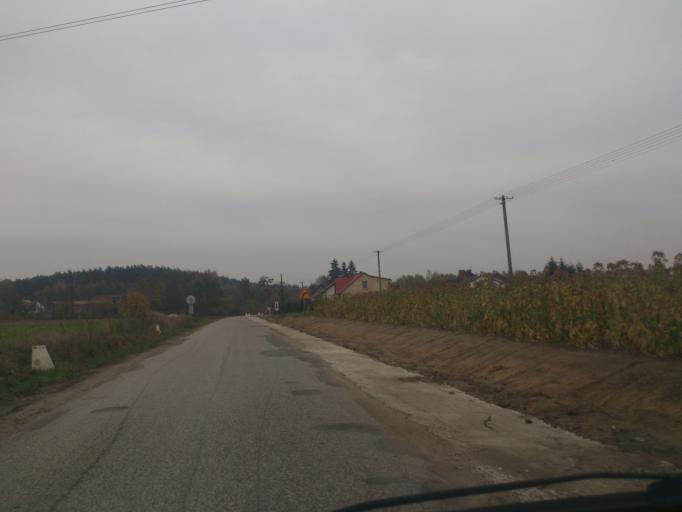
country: PL
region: Kujawsko-Pomorskie
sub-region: Powiat golubsko-dobrzynski
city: Golub-Dobrzyn
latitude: 53.1320
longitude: 19.0920
